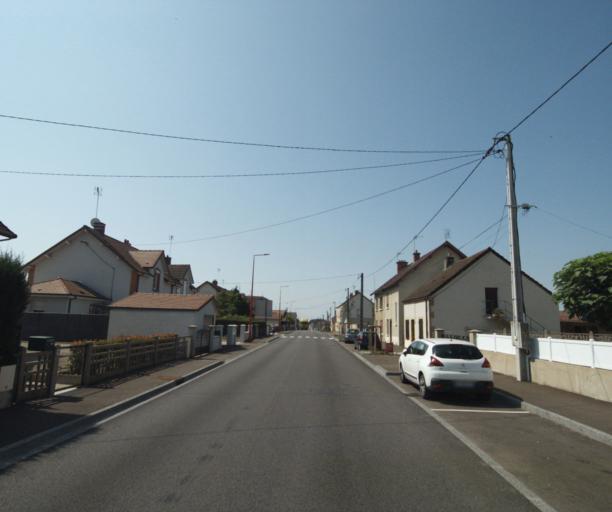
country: FR
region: Bourgogne
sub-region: Departement de Saone-et-Loire
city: Gueugnon
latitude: 46.6006
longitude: 4.0688
